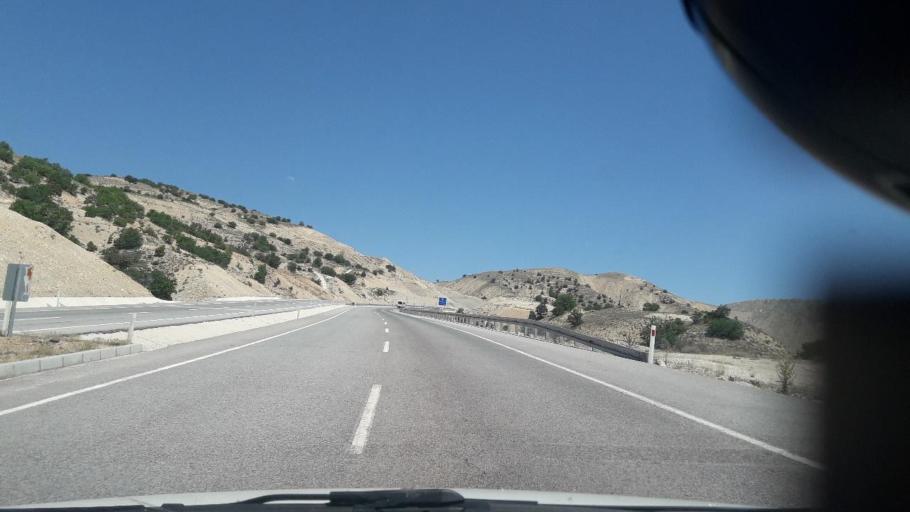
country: TR
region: Malatya
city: Hekimhan
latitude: 38.7387
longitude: 38.0019
